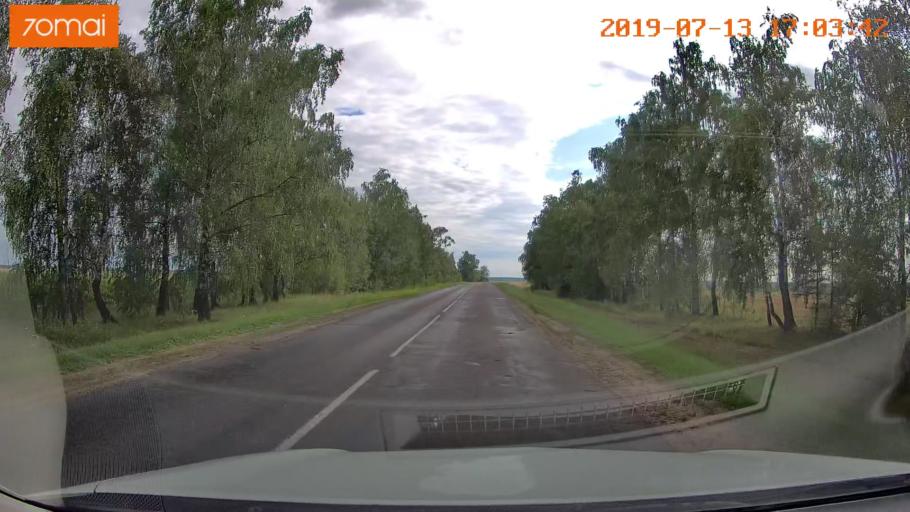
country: BY
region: Mogilev
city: Kirawsk
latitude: 53.2741
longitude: 29.3753
